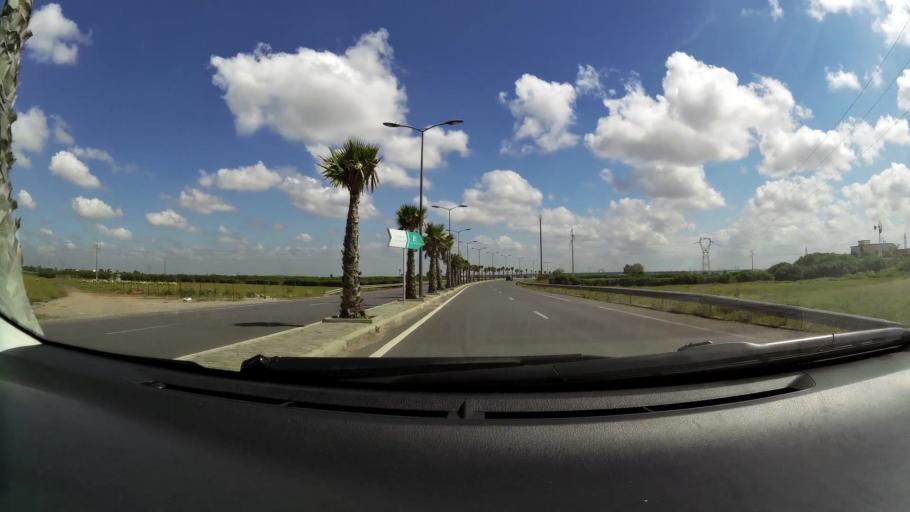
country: MA
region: Grand Casablanca
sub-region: Nouaceur
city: Bouskoura
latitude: 33.5046
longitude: -7.6099
